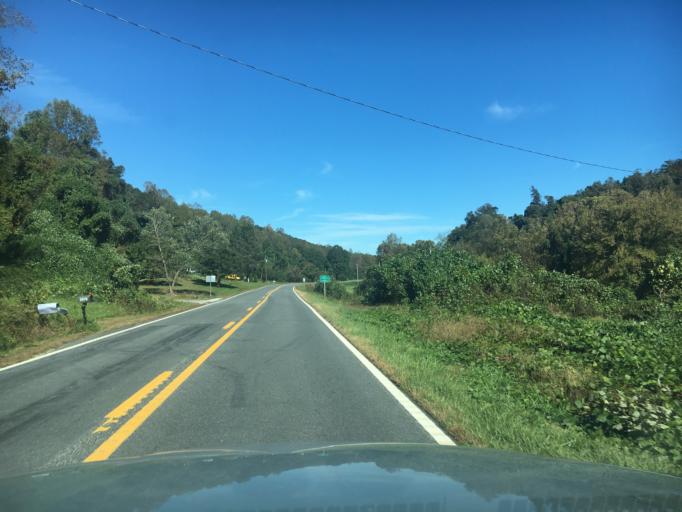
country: US
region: North Carolina
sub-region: Rutherford County
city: Spindale
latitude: 35.5403
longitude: -81.8565
